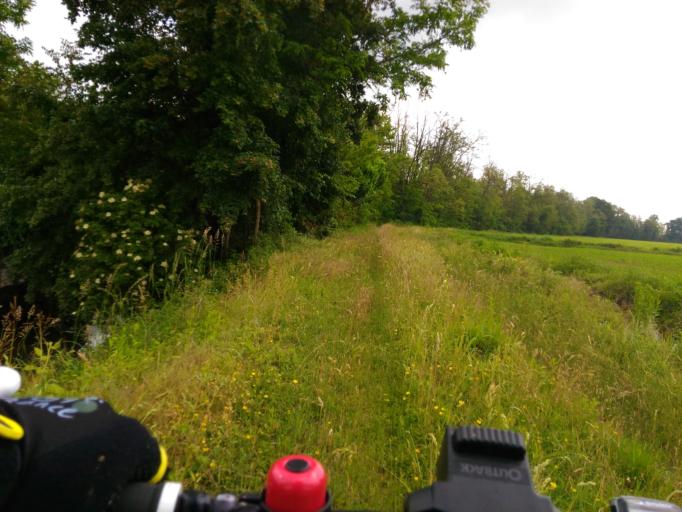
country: IT
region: Lombardy
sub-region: Provincia di Lodi
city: Turano Lodigiano
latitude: 45.2513
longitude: 9.6108
